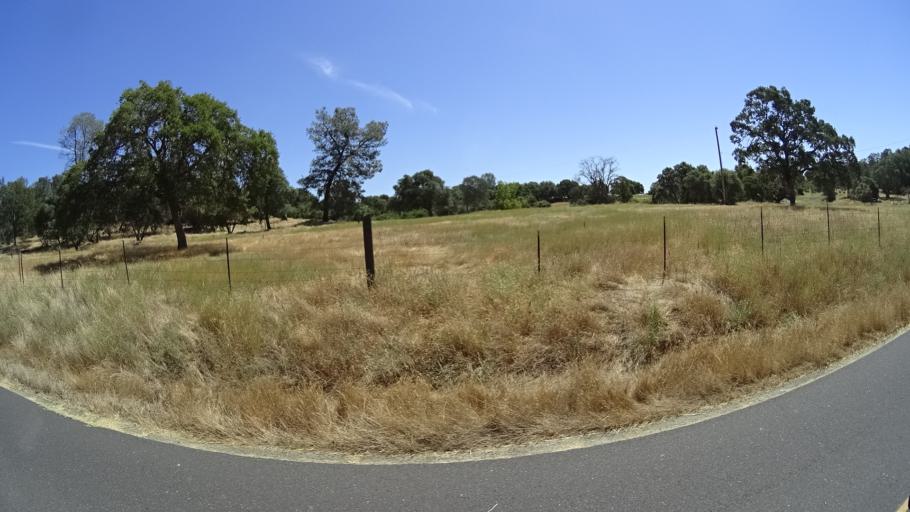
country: US
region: California
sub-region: Calaveras County
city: Angels Camp
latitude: 38.0903
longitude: -120.5564
